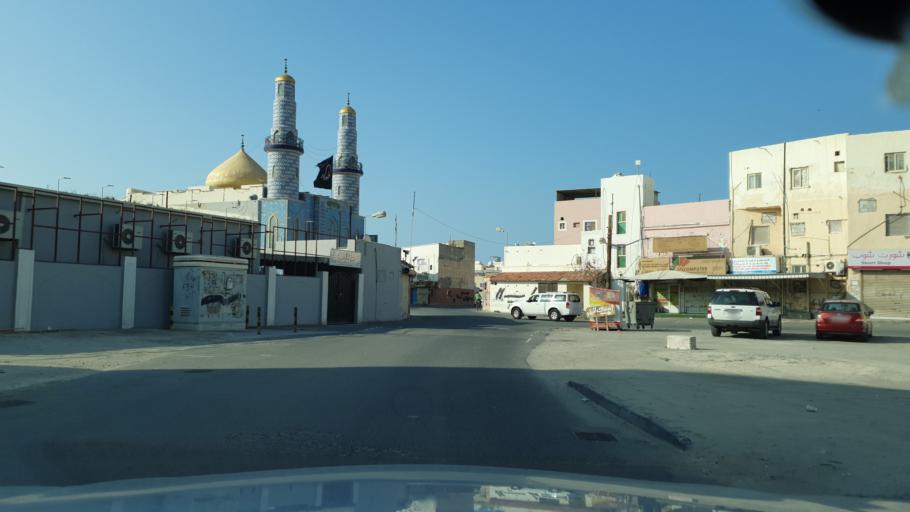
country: BH
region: Manama
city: Jidd Hafs
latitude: 26.2179
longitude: 50.4665
